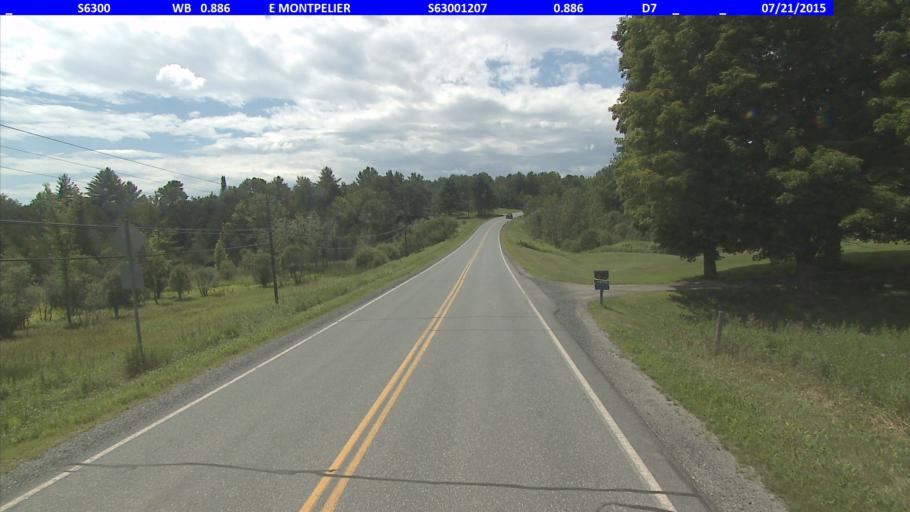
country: US
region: Vermont
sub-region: Washington County
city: Montpelier
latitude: 44.2530
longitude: -72.5236
